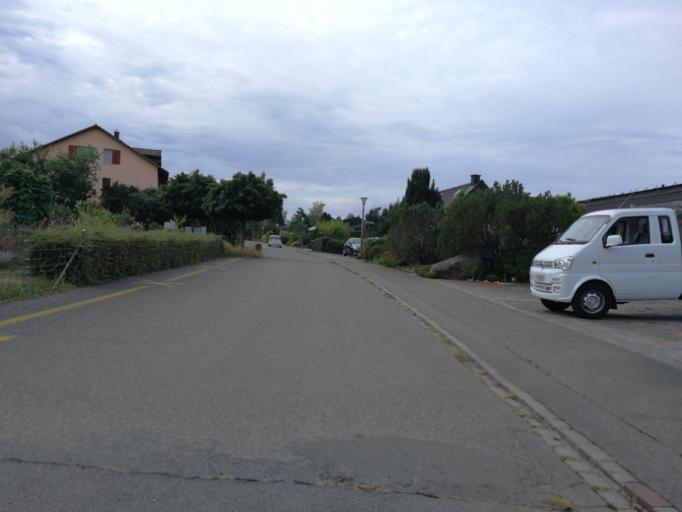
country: CH
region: Zurich
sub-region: Bezirk Hinwil
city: Wetzikon / Robenhausen
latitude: 47.3338
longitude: 8.7621
